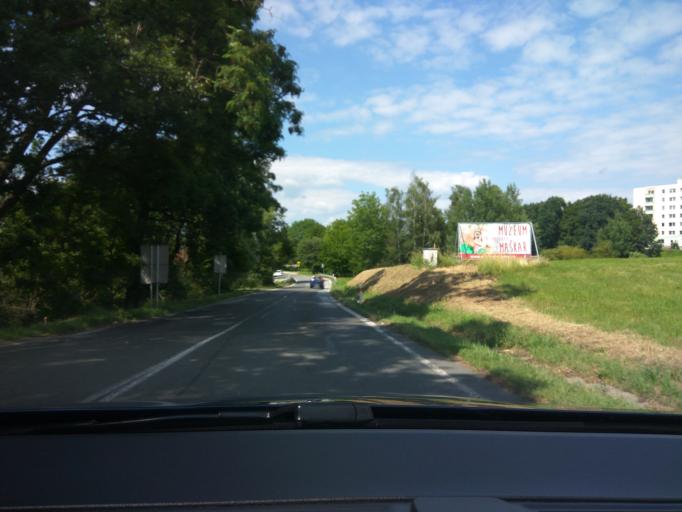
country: CZ
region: Jihocesky
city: Milevsko
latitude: 49.4424
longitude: 14.3594
